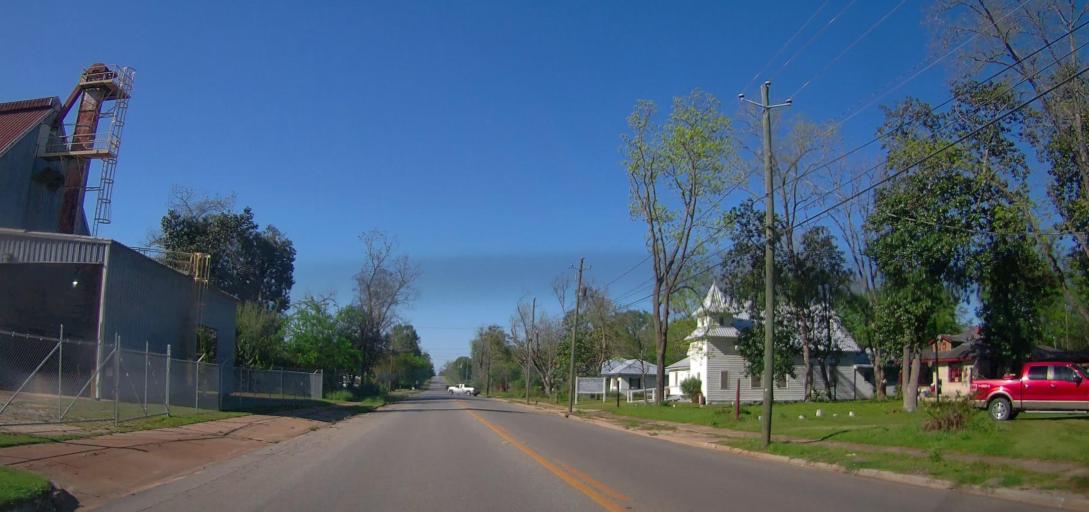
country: US
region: Georgia
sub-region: Wilcox County
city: Rochelle
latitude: 31.9525
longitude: -83.4563
